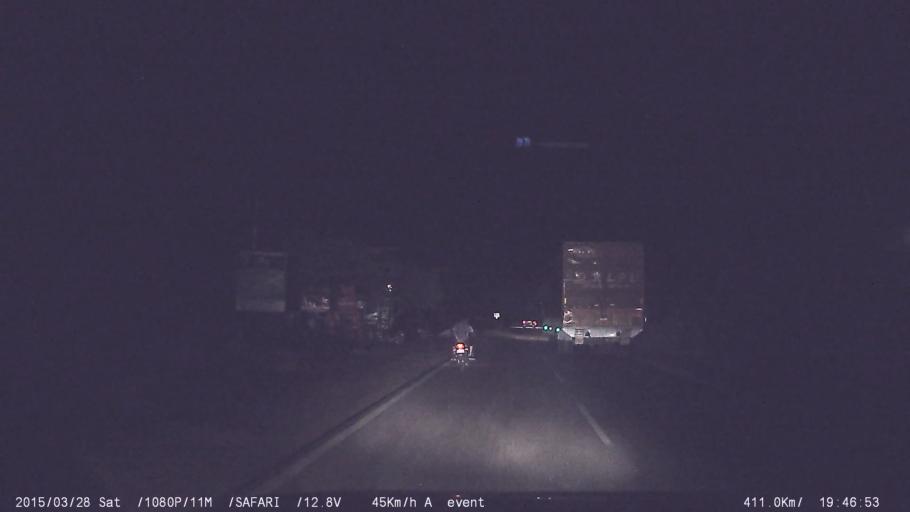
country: IN
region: Karnataka
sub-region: Mandya
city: Pandavapura
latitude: 12.4875
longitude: 76.7808
